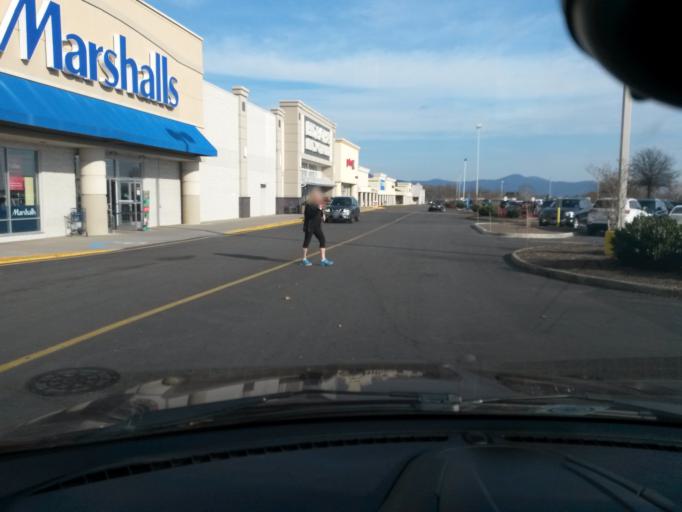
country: US
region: Virginia
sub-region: Roanoke County
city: Hollins
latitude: 37.3198
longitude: -79.9647
